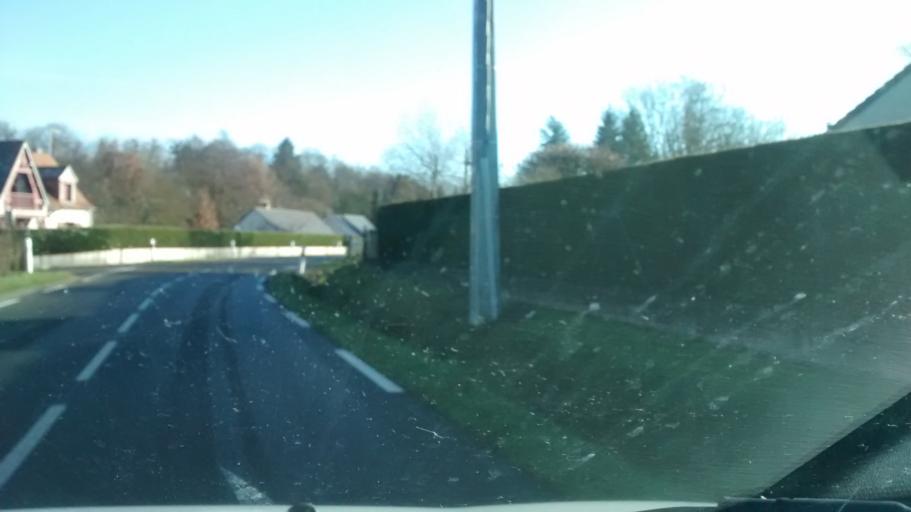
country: FR
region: Centre
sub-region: Departement d'Indre-et-Loire
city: Reugny
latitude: 47.4849
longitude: 0.8608
